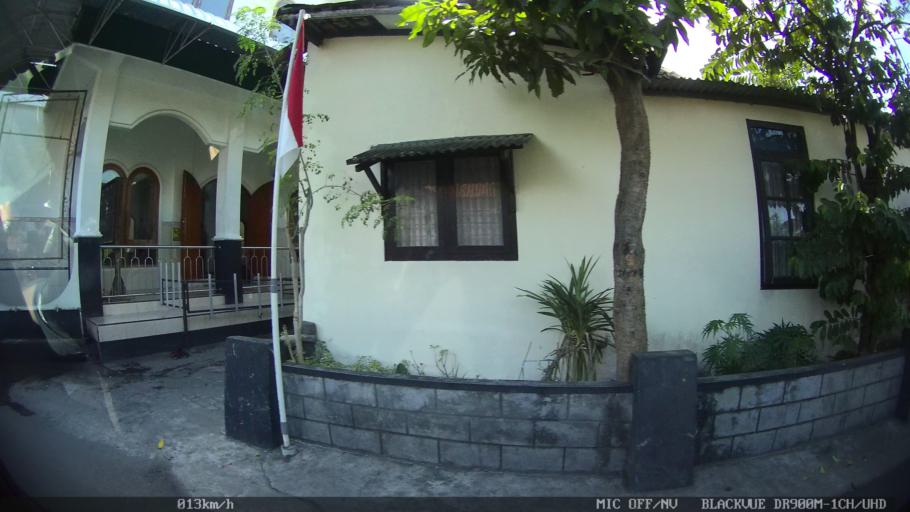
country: ID
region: Daerah Istimewa Yogyakarta
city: Kasihan
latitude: -7.8295
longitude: 110.3707
